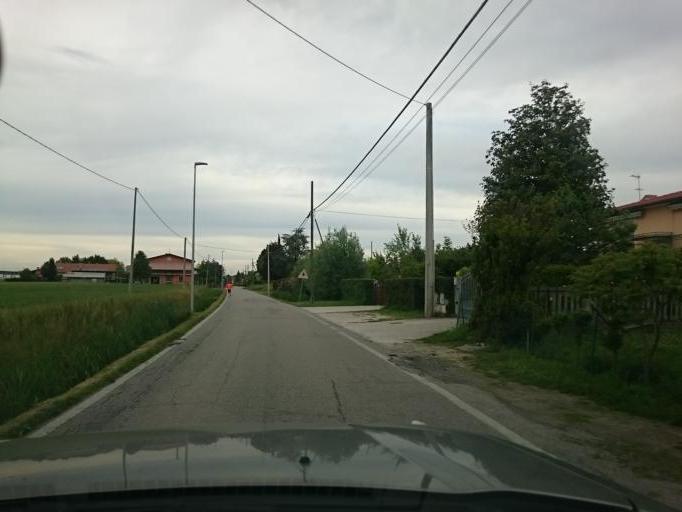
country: IT
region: Veneto
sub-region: Provincia di Padova
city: Bertipaglia
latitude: 45.3081
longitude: 11.8778
